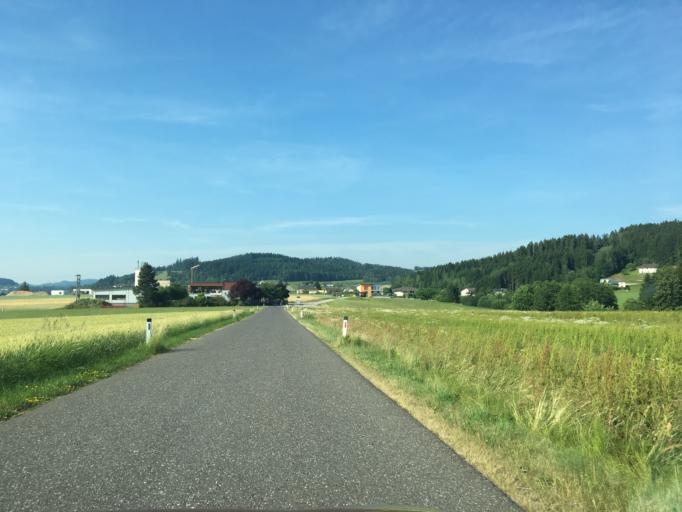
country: AT
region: Upper Austria
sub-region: Politischer Bezirk Urfahr-Umgebung
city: Herzogsdorf
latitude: 48.4217
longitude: 14.1575
